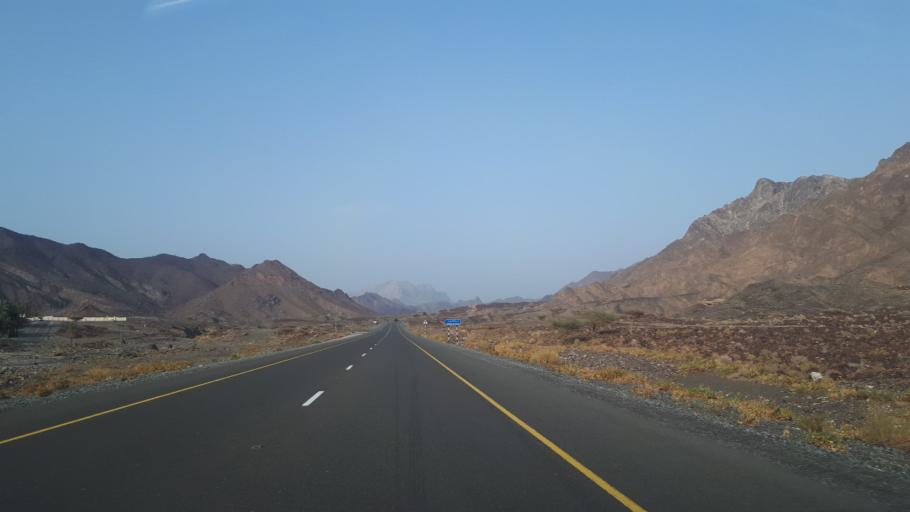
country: OM
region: Az Zahirah
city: Yanqul
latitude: 23.4936
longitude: 56.8806
